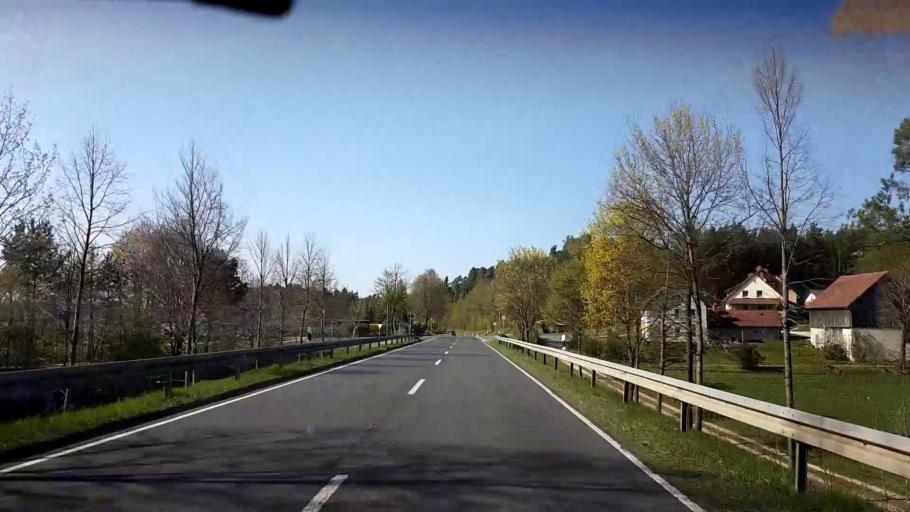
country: DE
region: Bavaria
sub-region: Upper Franconia
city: Plankenfels
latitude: 49.9059
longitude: 11.3259
